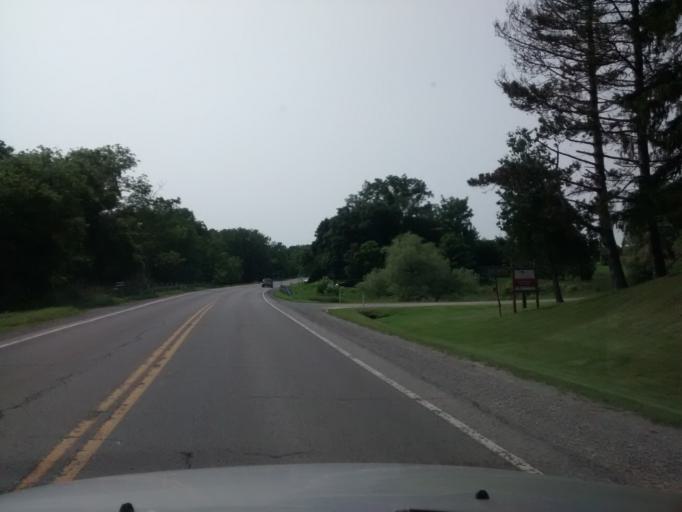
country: CA
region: Ontario
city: Ancaster
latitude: 43.0126
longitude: -79.8798
